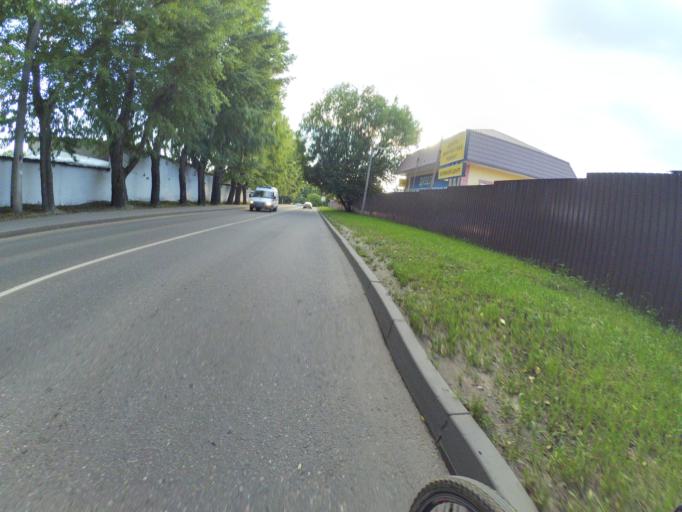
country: RU
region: Moscow
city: Strogino
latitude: 55.8381
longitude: 37.4310
